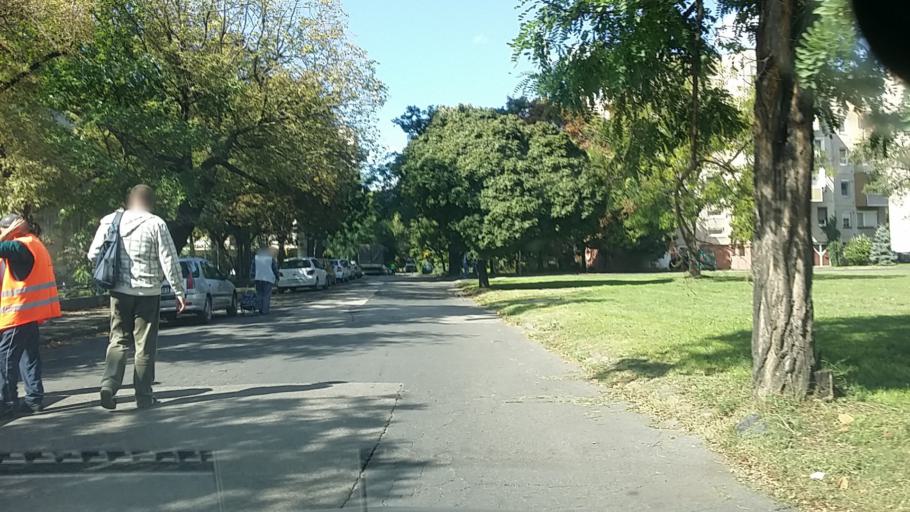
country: HU
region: Budapest
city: Budapest XV. keruelet
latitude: 47.5626
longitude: 19.1070
